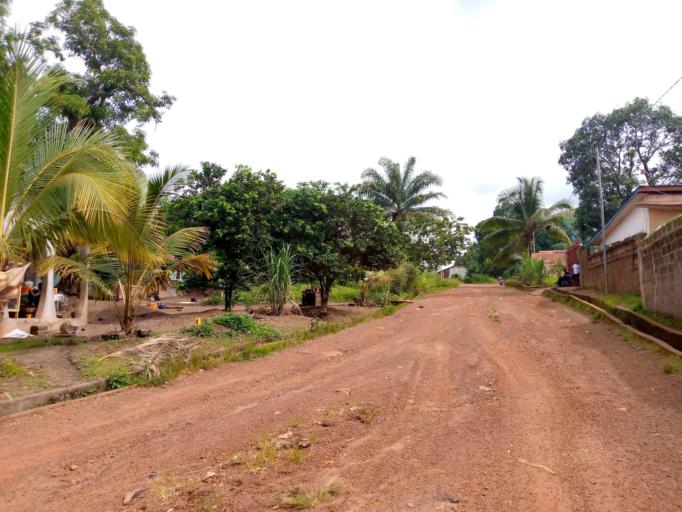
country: SL
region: Northern Province
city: Magburaka
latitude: 8.7229
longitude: -11.9388
